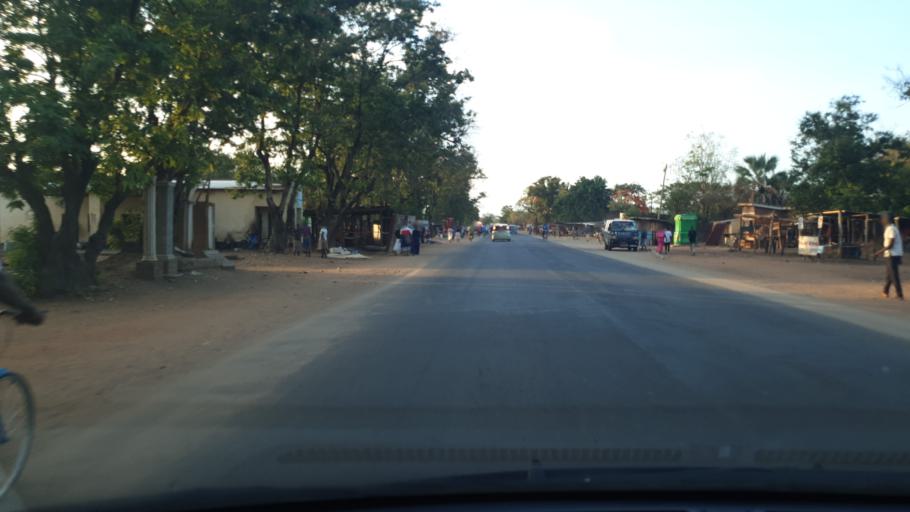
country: MW
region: Central Region
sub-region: Salima District
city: Salima
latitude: -13.7753
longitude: 34.4507
